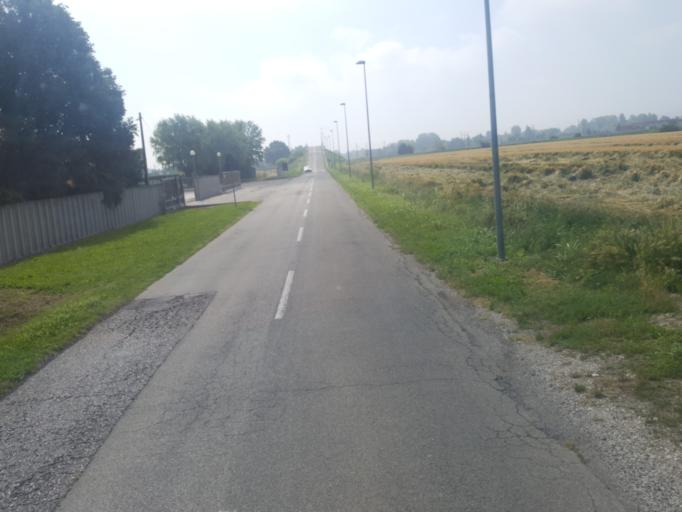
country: IT
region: Veneto
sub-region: Provincia di Rovigo
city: Canaro
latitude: 44.9292
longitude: 11.6824
